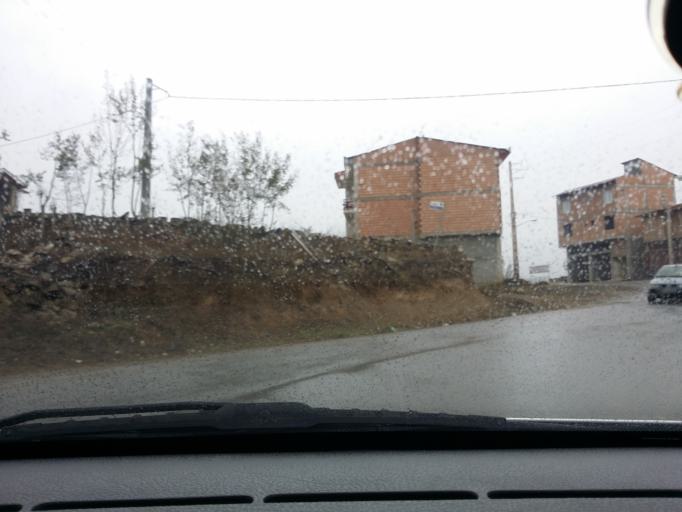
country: IR
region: Mazandaran
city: Chalus
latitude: 36.5238
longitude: 51.2338
